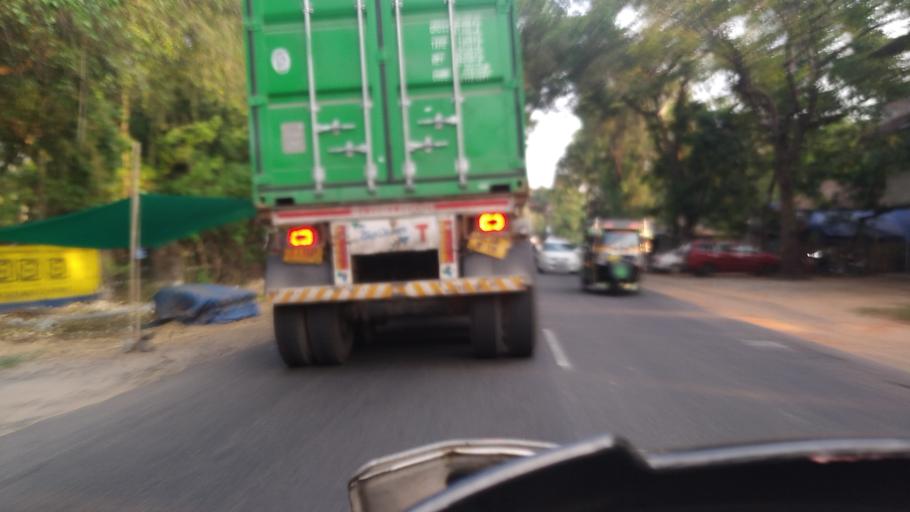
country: IN
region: Kerala
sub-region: Thrissur District
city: Thanniyam
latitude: 10.3458
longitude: 76.1347
